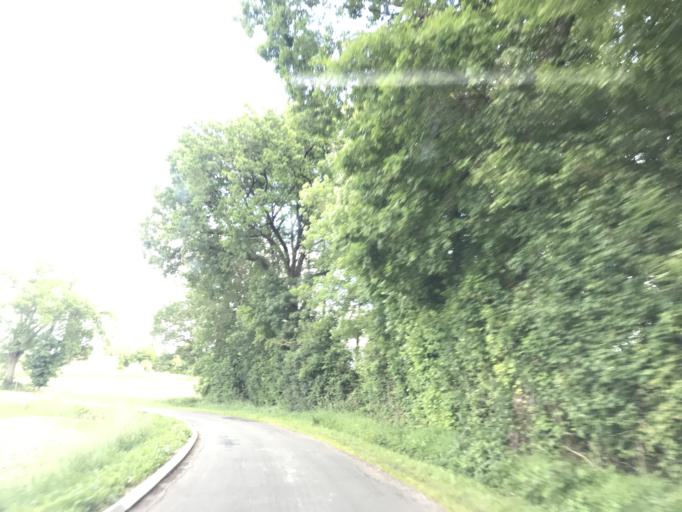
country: FR
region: Aquitaine
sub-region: Departement de la Dordogne
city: Saint-Aulaye
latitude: 45.2612
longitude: 0.1283
